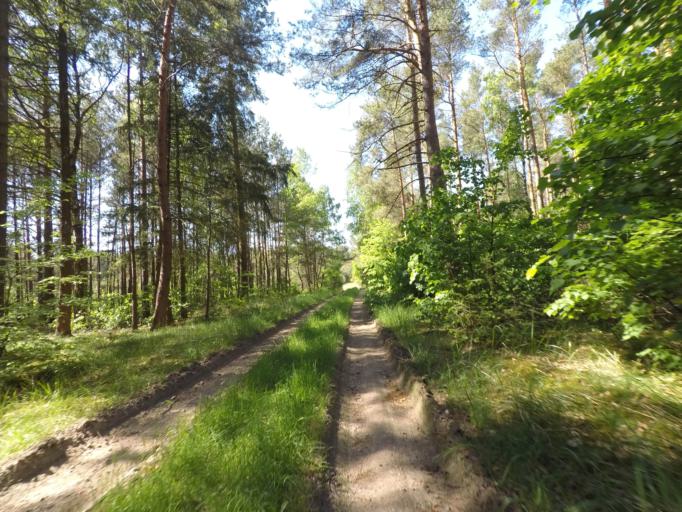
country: DE
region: Brandenburg
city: Melchow
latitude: 52.8235
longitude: 13.7496
